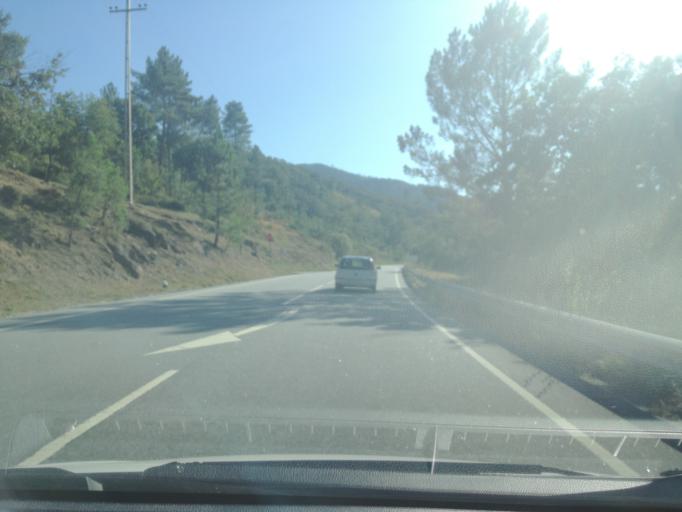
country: ES
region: Galicia
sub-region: Provincia de Ourense
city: Entrimo
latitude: 41.8724
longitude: -8.1743
